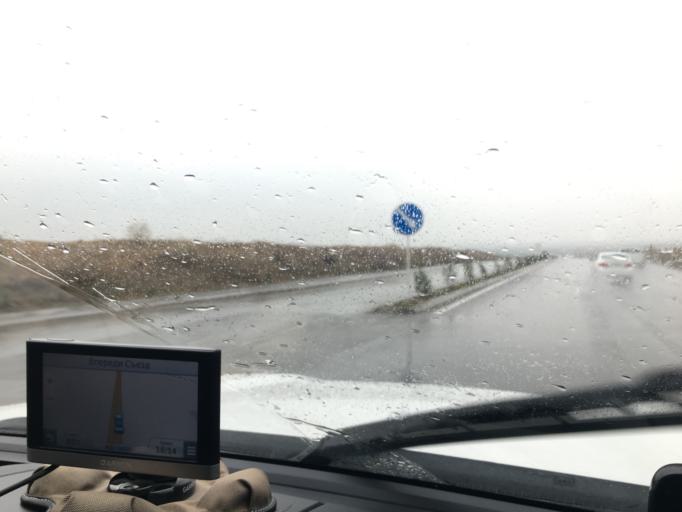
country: TM
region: Ahal
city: Annau
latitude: 37.8875
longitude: 58.6206
